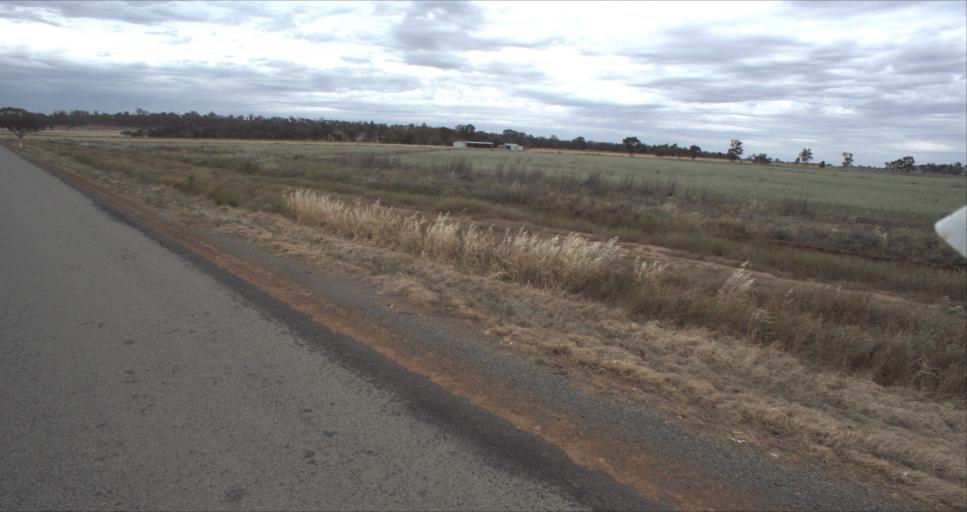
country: AU
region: New South Wales
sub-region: Leeton
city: Leeton
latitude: -34.4313
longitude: 146.3171
